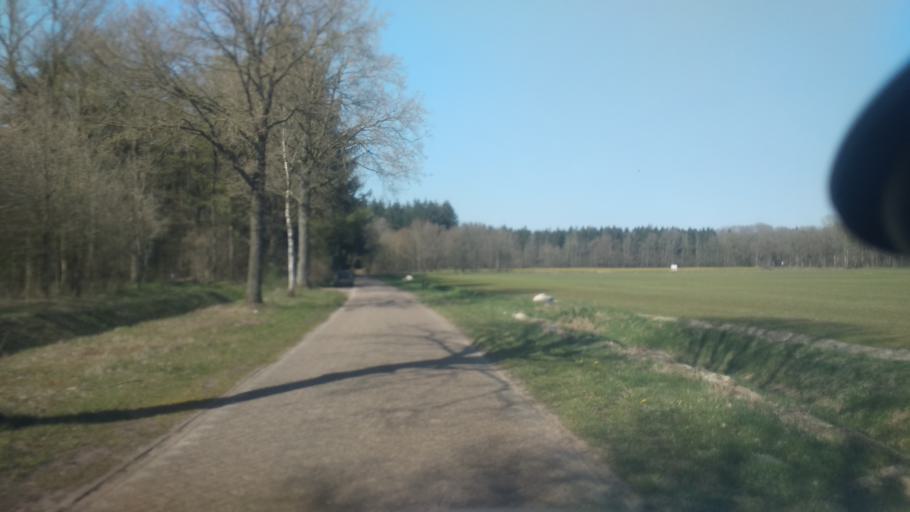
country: NL
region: Drenthe
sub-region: Gemeente Borger-Odoorn
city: Borger
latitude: 52.9294
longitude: 6.7365
